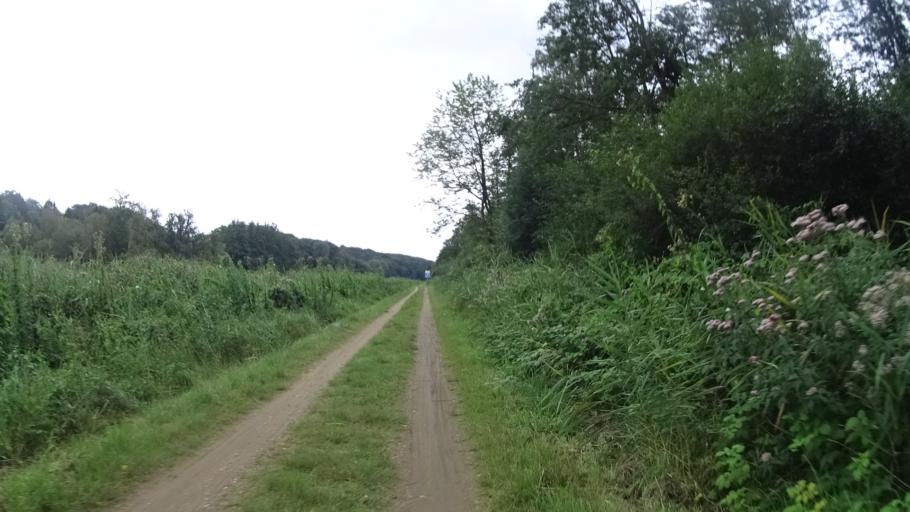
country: DE
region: Schleswig-Holstein
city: Alt Molln
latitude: 53.6408
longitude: 10.6566
